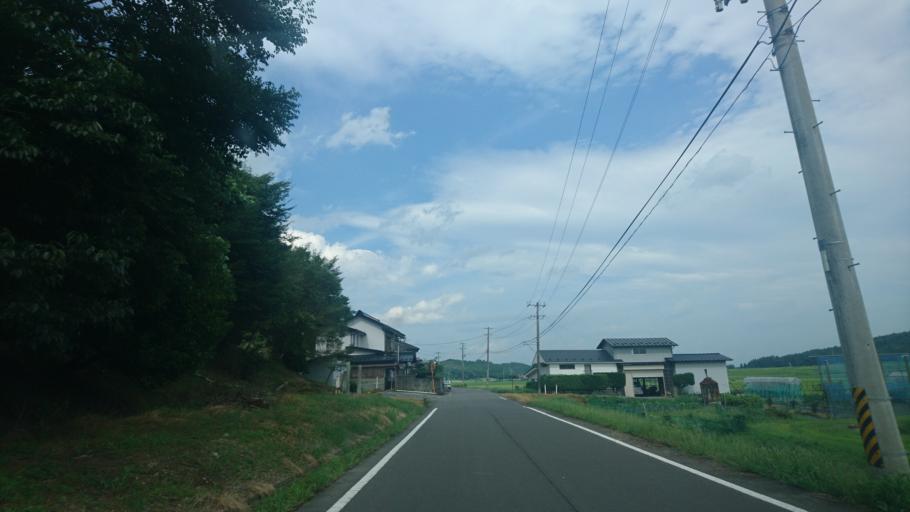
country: JP
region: Miyagi
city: Furukawa
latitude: 38.7646
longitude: 140.9835
